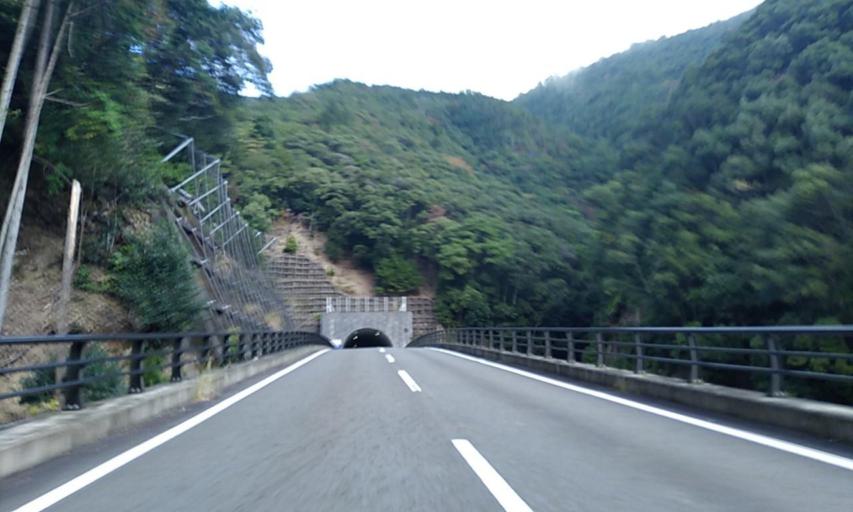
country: JP
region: Wakayama
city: Shingu
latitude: 33.8798
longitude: 135.8768
